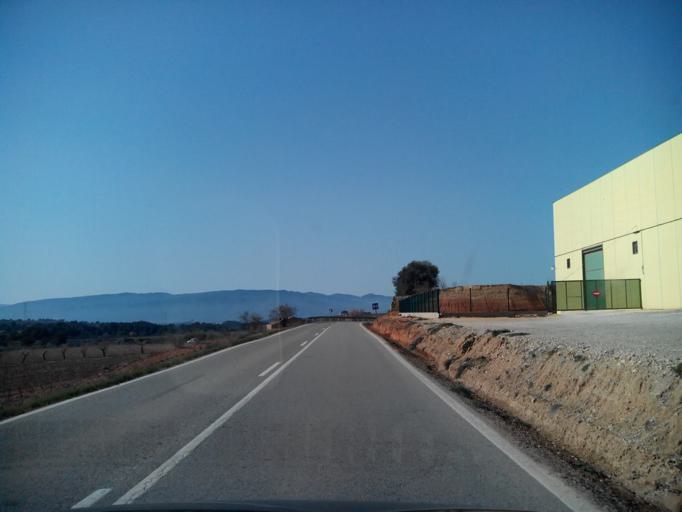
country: ES
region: Catalonia
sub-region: Provincia de Tarragona
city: Fores
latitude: 41.4432
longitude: 1.2397
